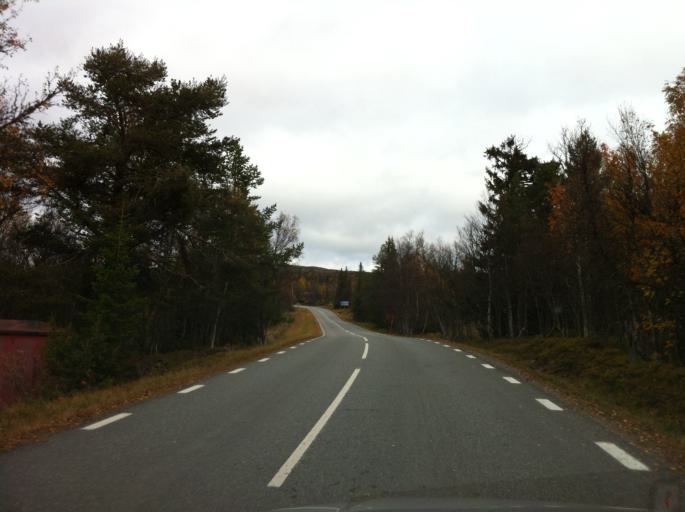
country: NO
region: Hedmark
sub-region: Engerdal
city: Engerdal
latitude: 62.0928
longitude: 12.3078
